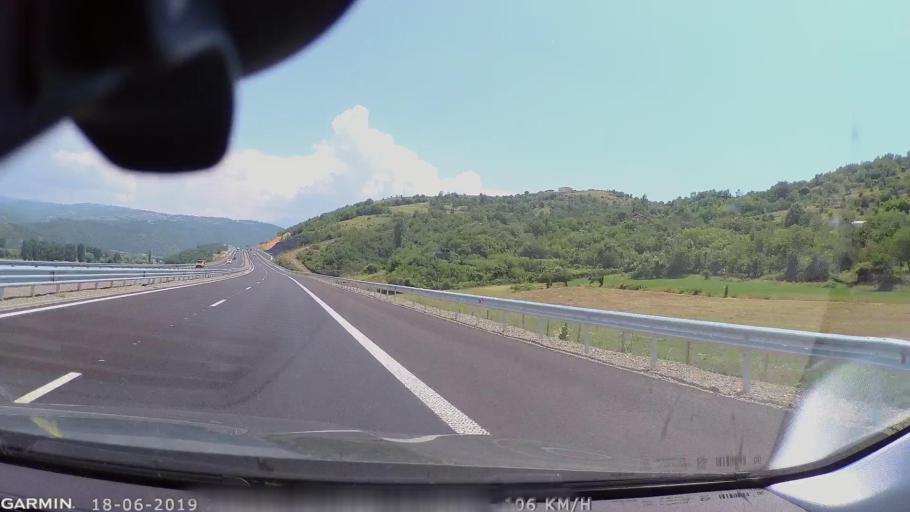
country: BG
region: Blagoevgrad
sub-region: Obshtina Blagoevgrad
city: Blagoevgrad
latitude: 41.9782
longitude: 23.0671
